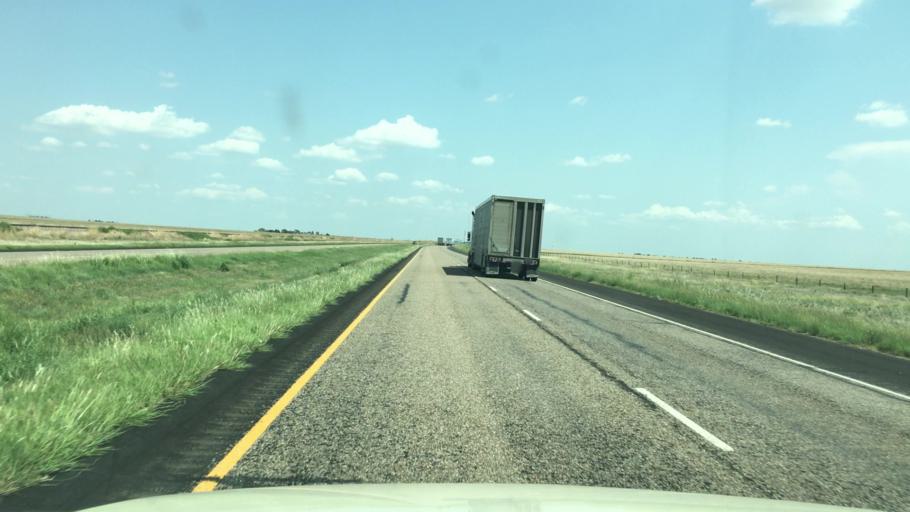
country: US
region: Texas
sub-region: Armstrong County
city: Claude
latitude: 35.1275
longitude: -101.4035
